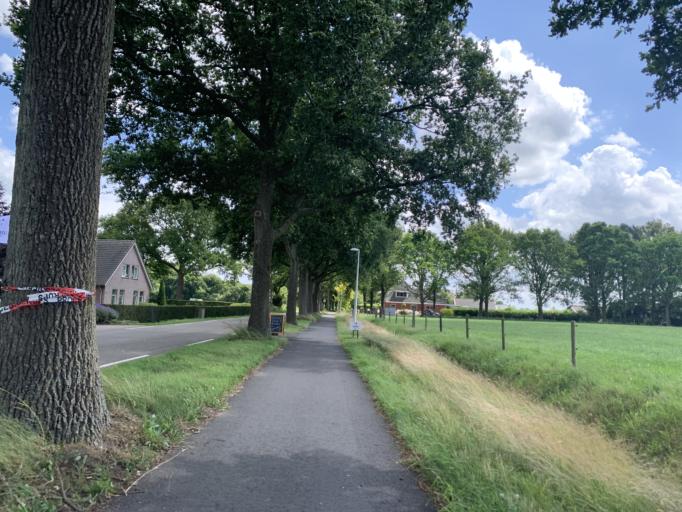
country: NL
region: Groningen
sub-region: Gemeente Haren
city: Haren
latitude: 53.1510
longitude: 6.6460
